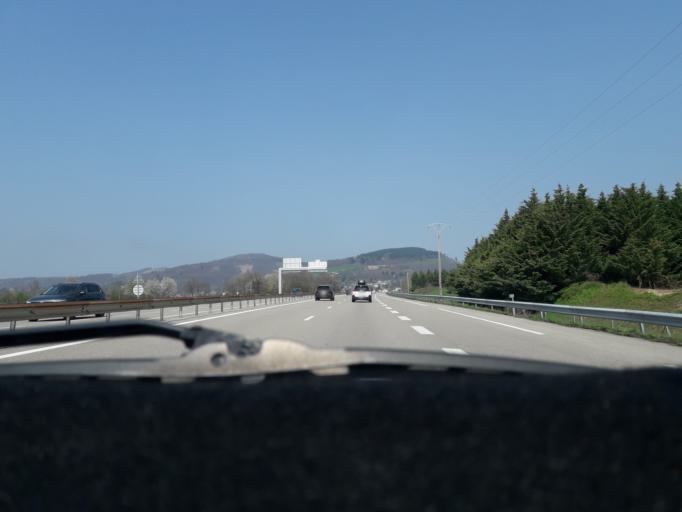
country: FR
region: Rhone-Alpes
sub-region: Departement de l'Isere
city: Colombe
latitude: 45.3886
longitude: 5.4713
